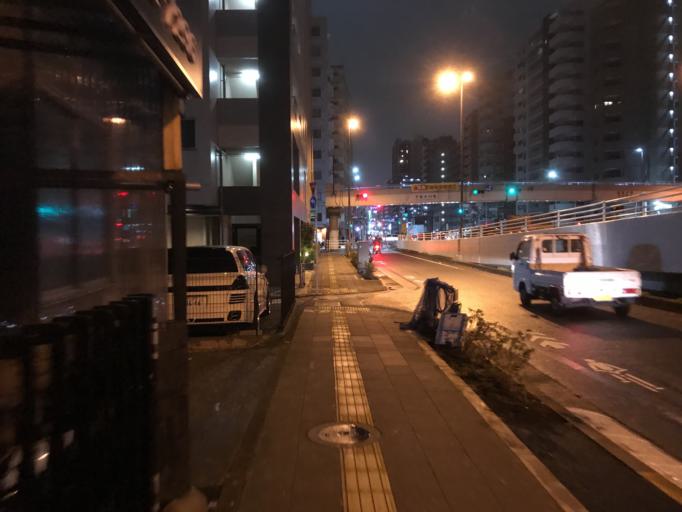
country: JP
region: Saitama
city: Soka
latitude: 35.7554
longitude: 139.8018
